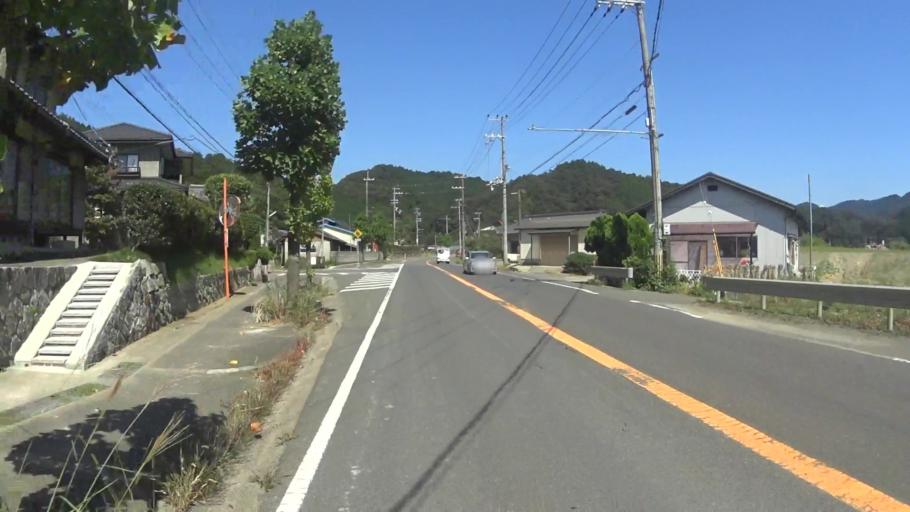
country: JP
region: Kyoto
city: Maizuru
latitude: 35.4564
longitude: 135.2703
